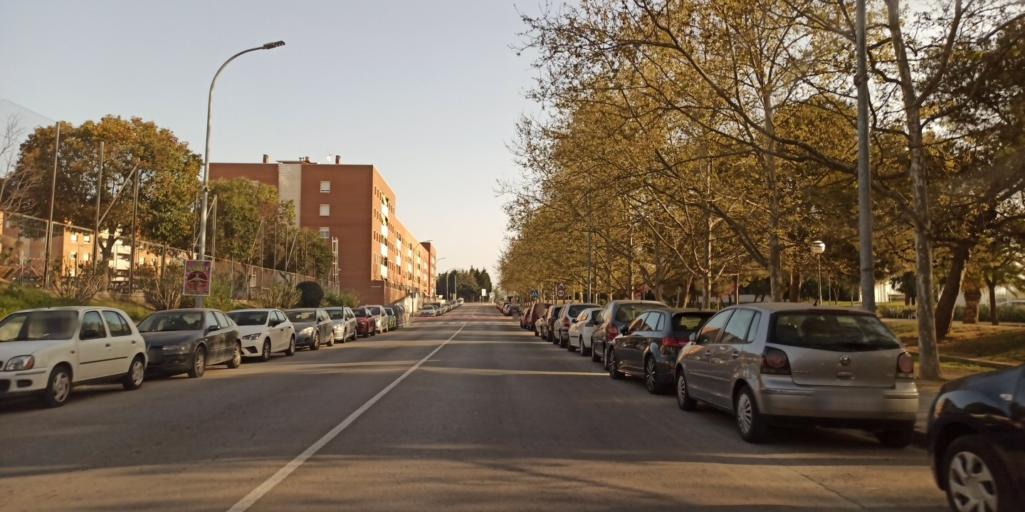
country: ES
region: Catalonia
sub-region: Provincia de Barcelona
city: Vilafranca del Penedes
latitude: 41.3518
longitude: 1.7059
